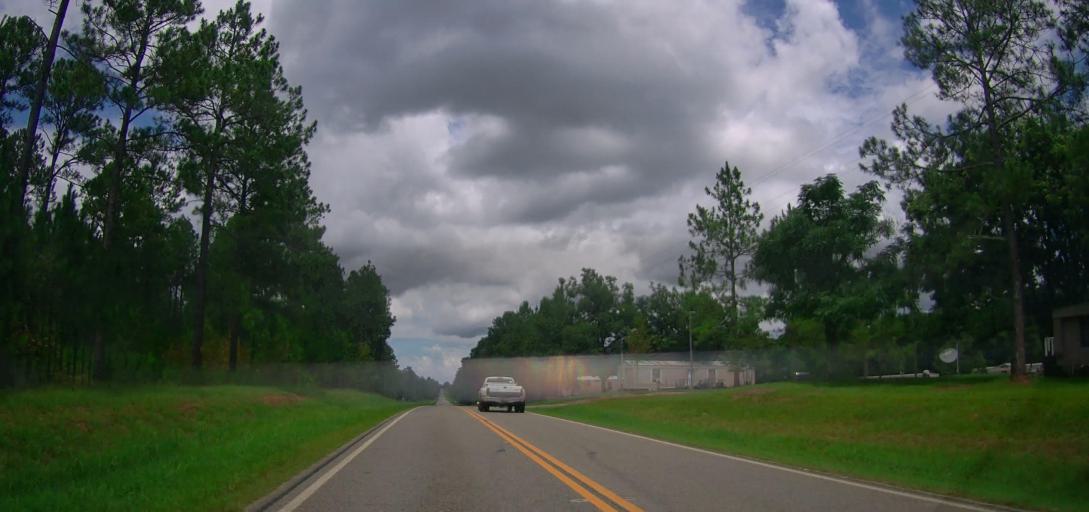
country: US
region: Georgia
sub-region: Wilcox County
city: Rochelle
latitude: 31.9029
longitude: -83.5531
